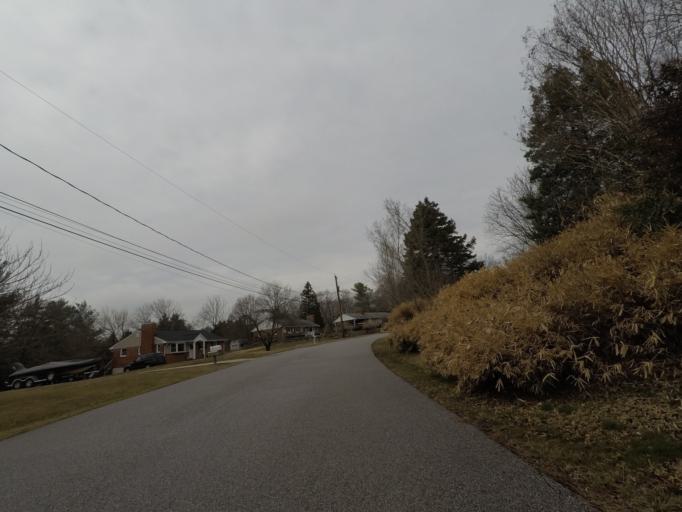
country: US
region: Maryland
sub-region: Howard County
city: Ilchester
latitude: 39.2202
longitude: -76.7846
